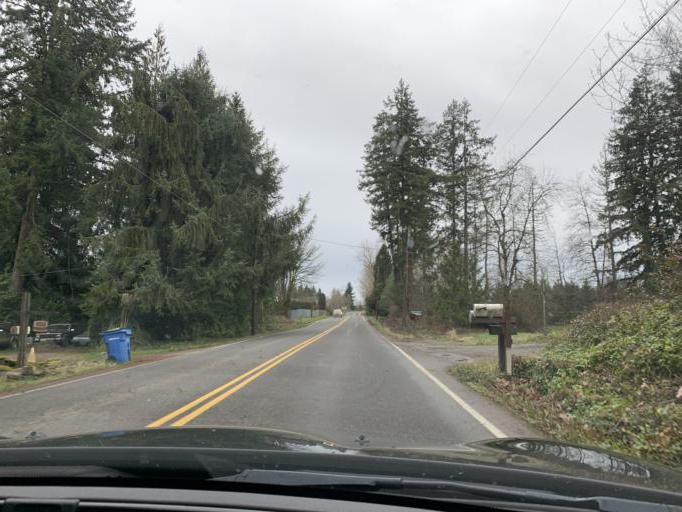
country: US
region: Washington
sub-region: Clark County
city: Barberton
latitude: 45.6862
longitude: -122.5931
